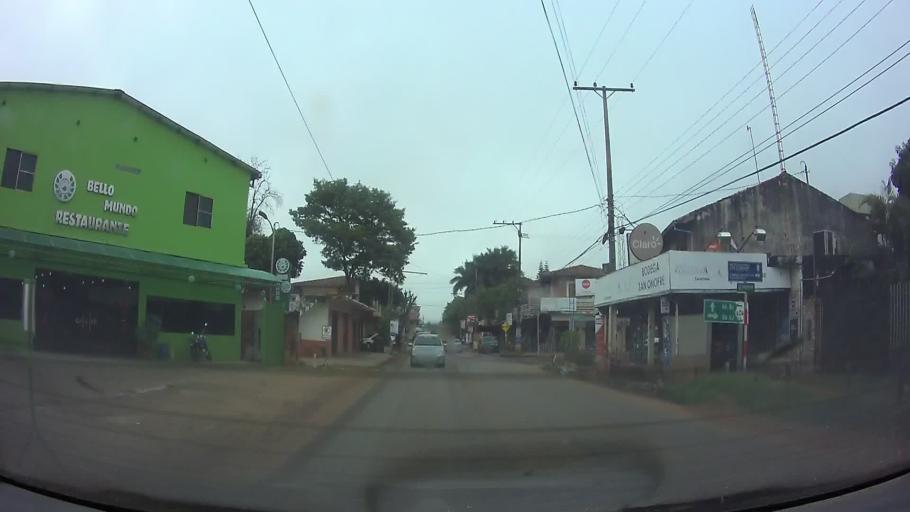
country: PY
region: Central
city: San Lorenzo
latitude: -25.3330
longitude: -57.5072
